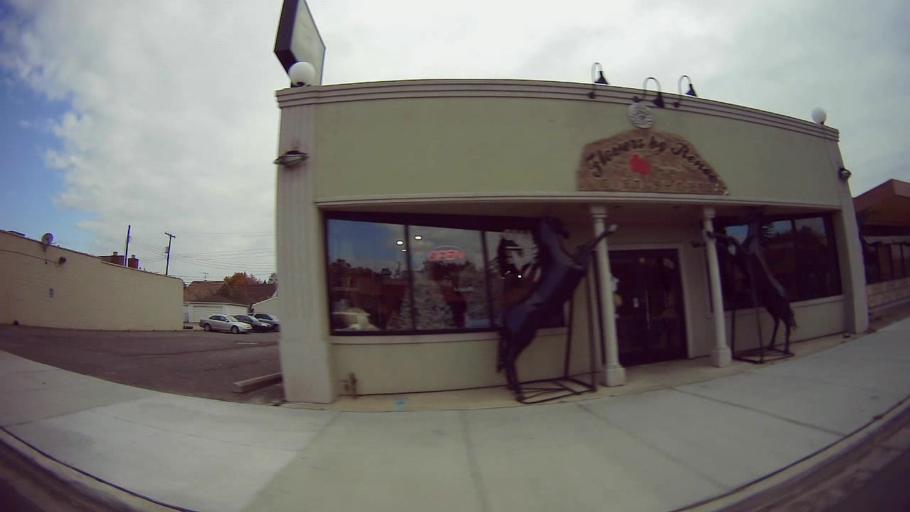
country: US
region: Michigan
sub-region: Wayne County
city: Dearborn
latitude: 42.3415
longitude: -83.1767
